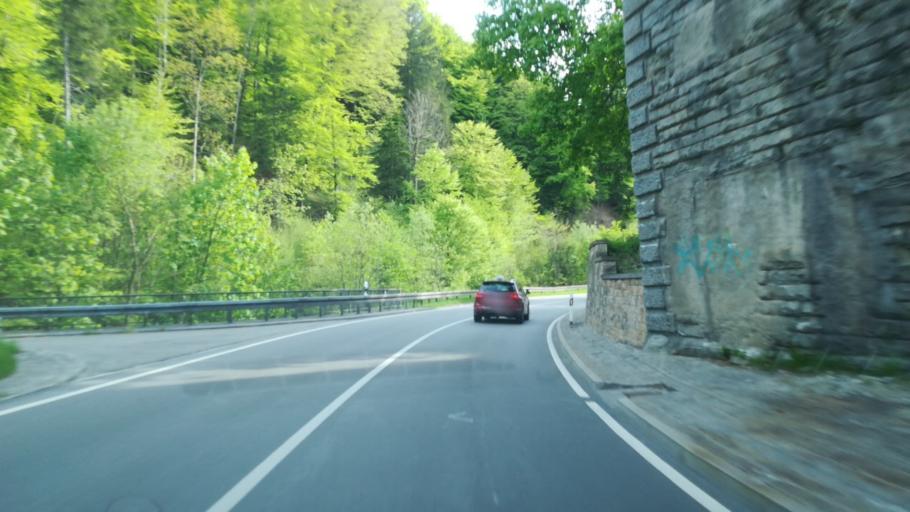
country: DE
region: Baden-Wuerttemberg
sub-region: Freiburg Region
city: Muhlingen
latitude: 47.9017
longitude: 9.0135
